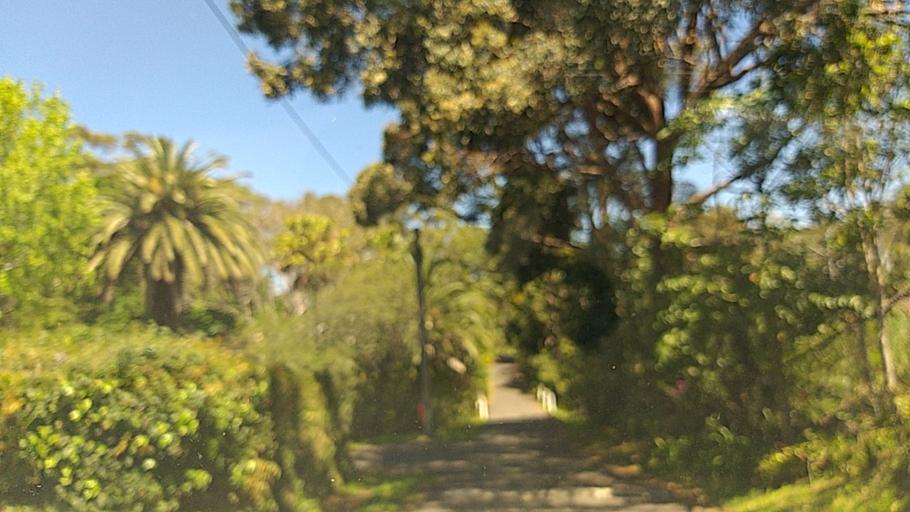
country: AU
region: New South Wales
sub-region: Wollongong
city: Bulli
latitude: -34.3048
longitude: 150.9318
